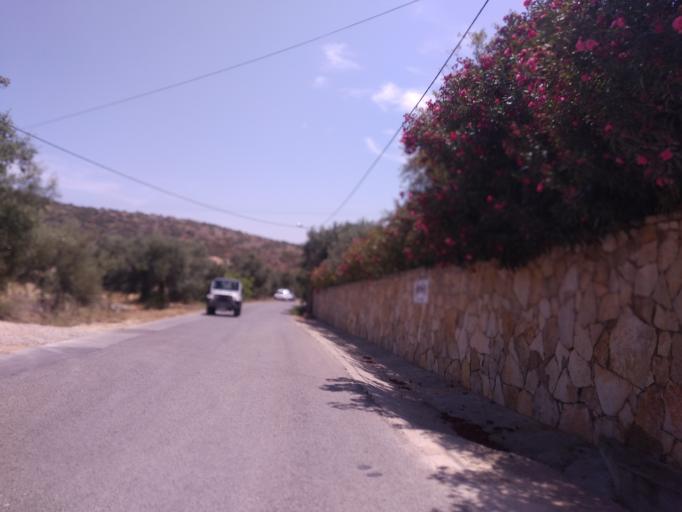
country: PT
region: Faro
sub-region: Faro
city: Santa Barbara de Nexe
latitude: 37.1124
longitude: -7.9462
